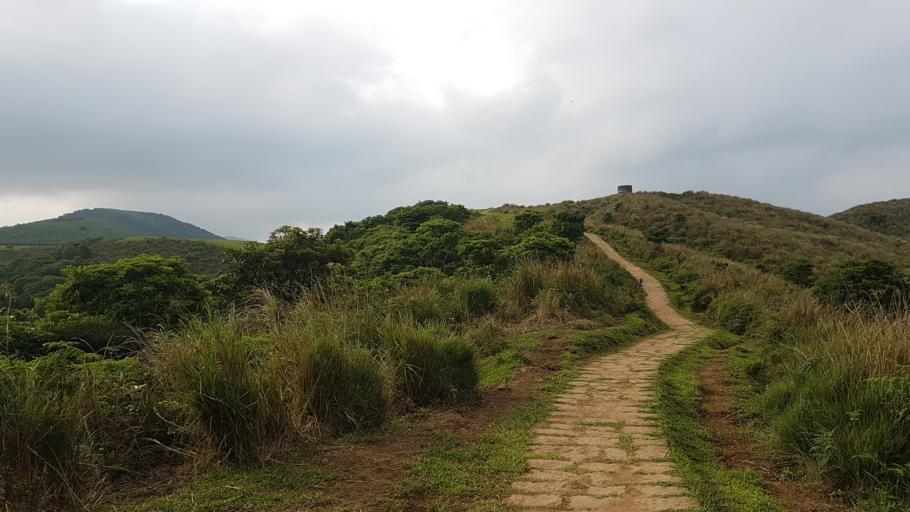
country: TW
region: Taipei
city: Taipei
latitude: 25.1624
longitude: 121.5783
